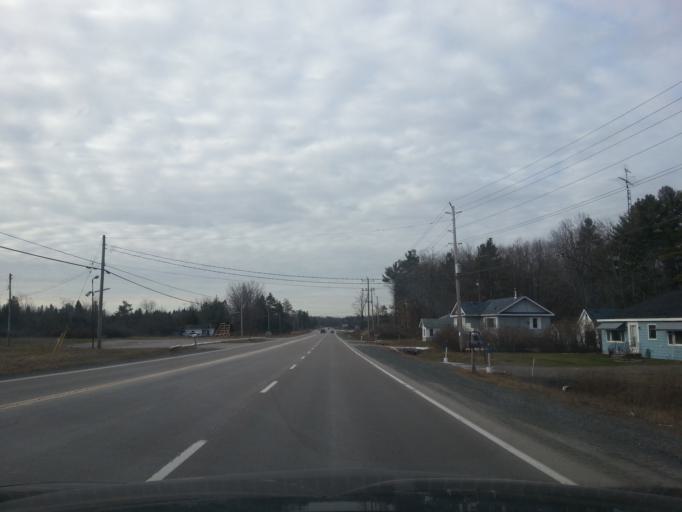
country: CA
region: Ontario
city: Quinte West
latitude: 44.4739
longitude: -77.7034
